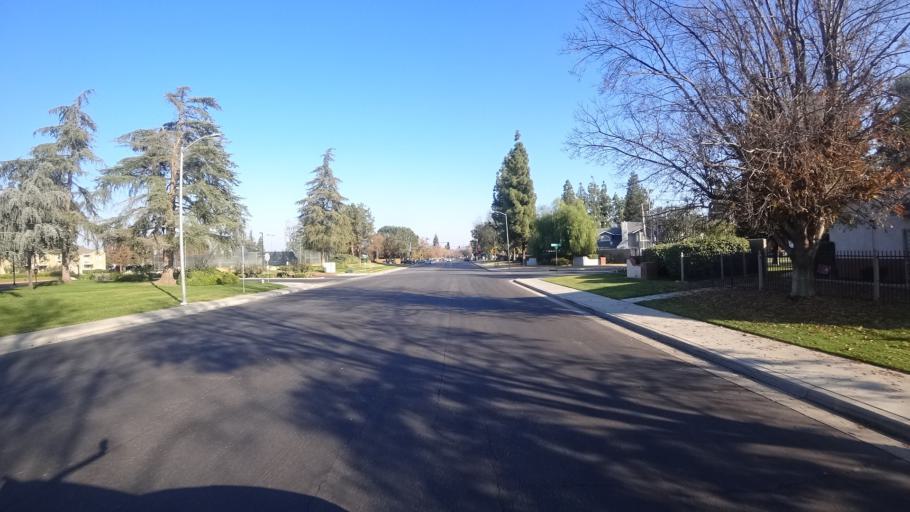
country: US
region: California
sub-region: Kern County
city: Greenacres
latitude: 35.3337
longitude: -119.0937
